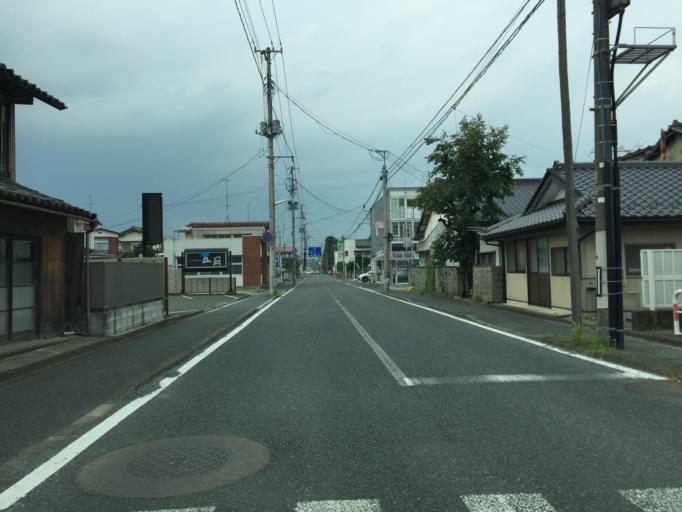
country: JP
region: Fukushima
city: Namie
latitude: 37.6394
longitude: 140.9624
